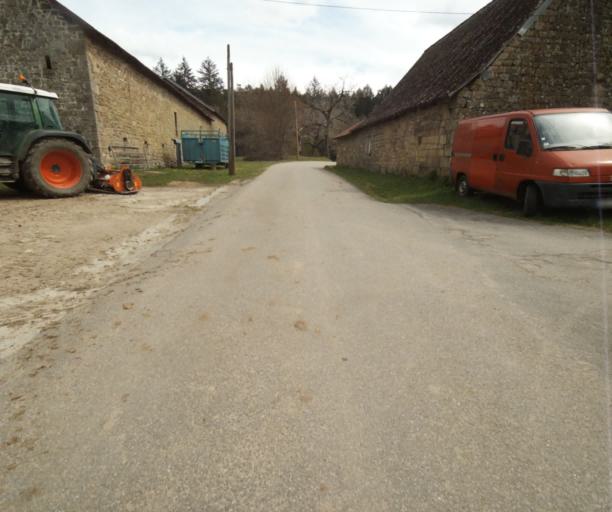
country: FR
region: Limousin
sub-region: Departement de la Correze
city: Correze
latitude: 45.3394
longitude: 1.9642
